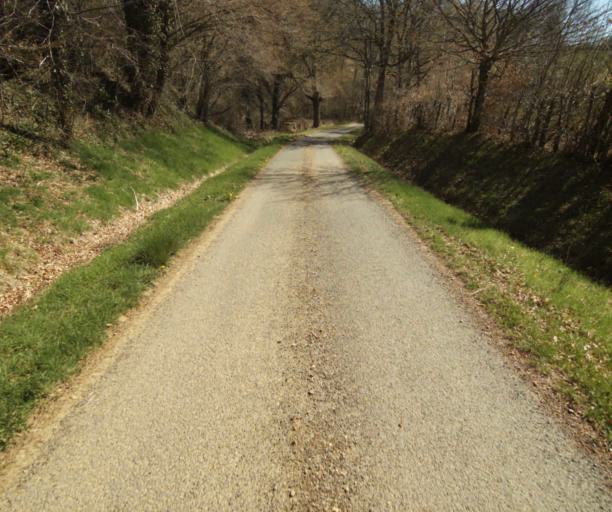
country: FR
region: Limousin
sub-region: Departement de la Correze
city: Chamboulive
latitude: 45.4588
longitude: 1.6762
